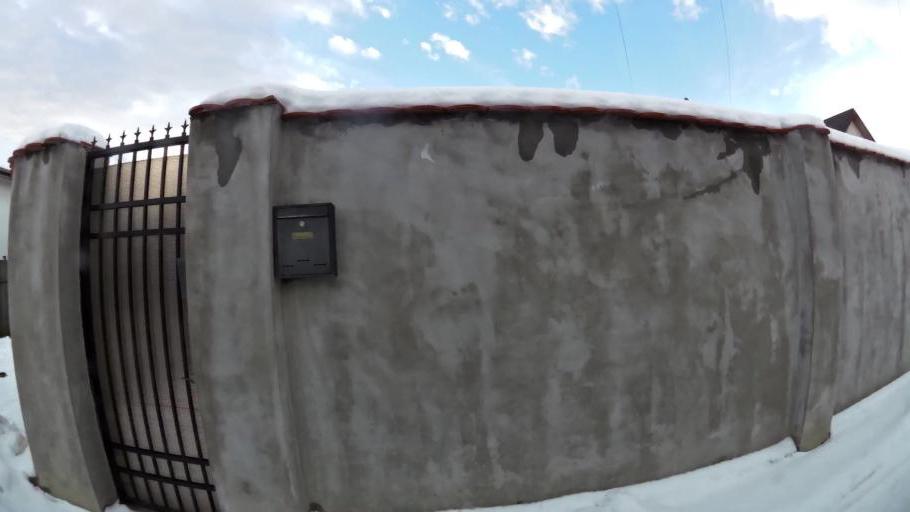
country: RO
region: Ilfov
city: Dobroesti
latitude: 44.4573
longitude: 26.1765
